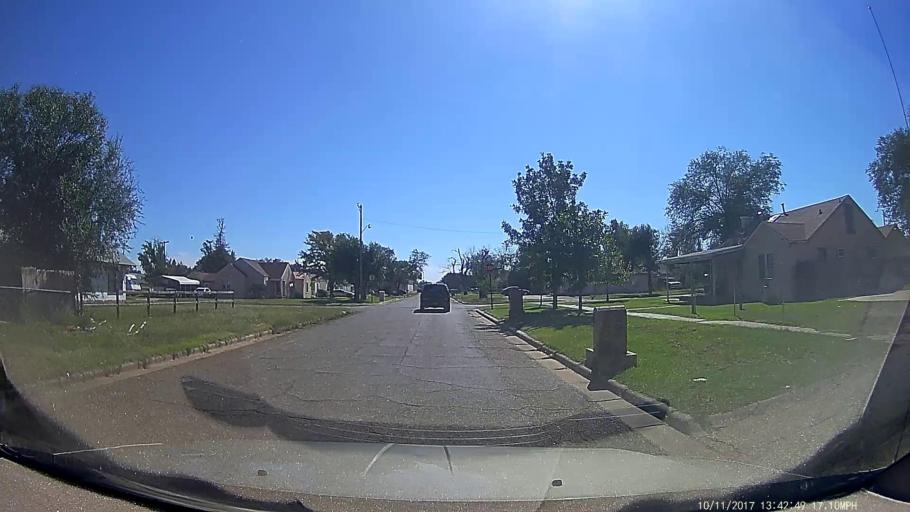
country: US
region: New Mexico
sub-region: Curry County
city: Clovis
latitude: 34.4069
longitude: -103.2130
